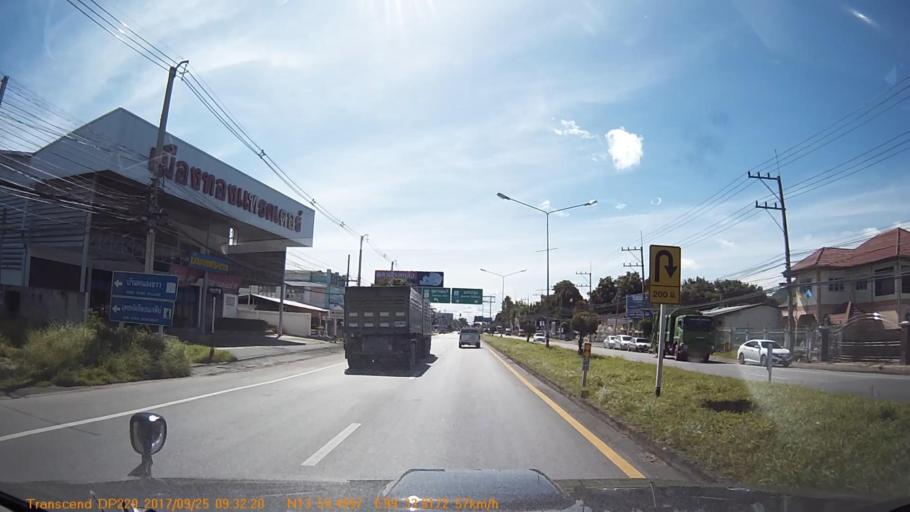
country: TH
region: Kanchanaburi
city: Kanchanaburi
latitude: 13.9916
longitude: 99.5653
